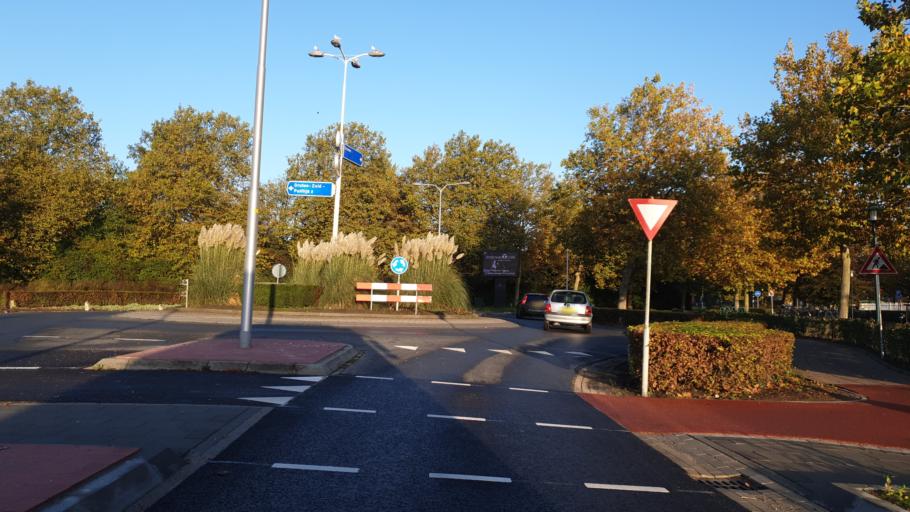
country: NL
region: Gelderland
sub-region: Gemeente Druten
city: Druten
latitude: 51.8844
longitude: 5.6055
